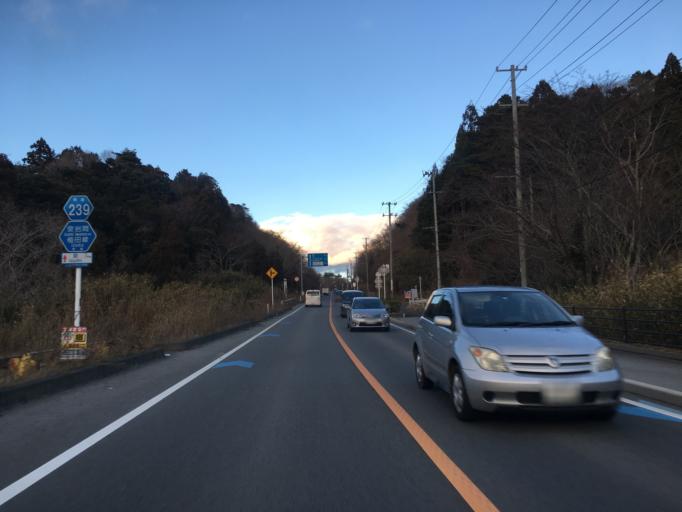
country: JP
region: Fukushima
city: Iwaki
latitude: 36.9143
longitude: 140.8387
